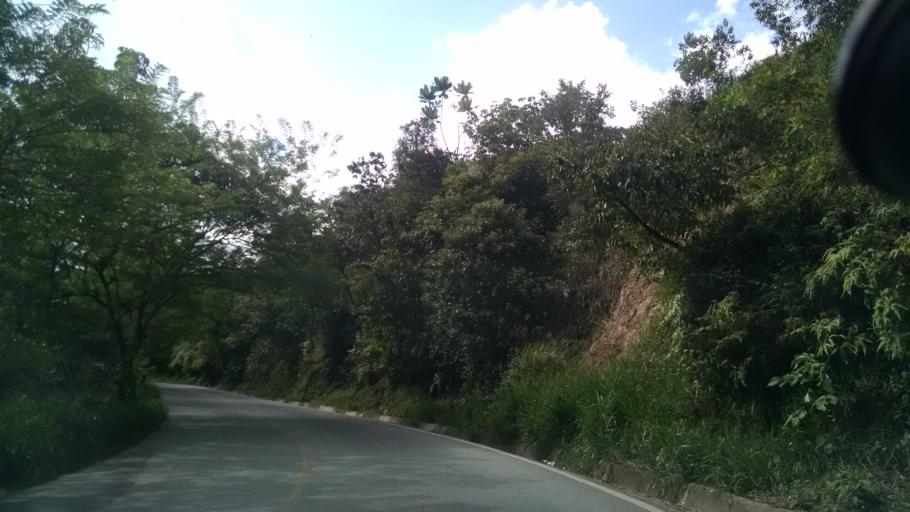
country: CO
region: Antioquia
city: Santo Domingo
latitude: 6.5359
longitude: -75.2326
